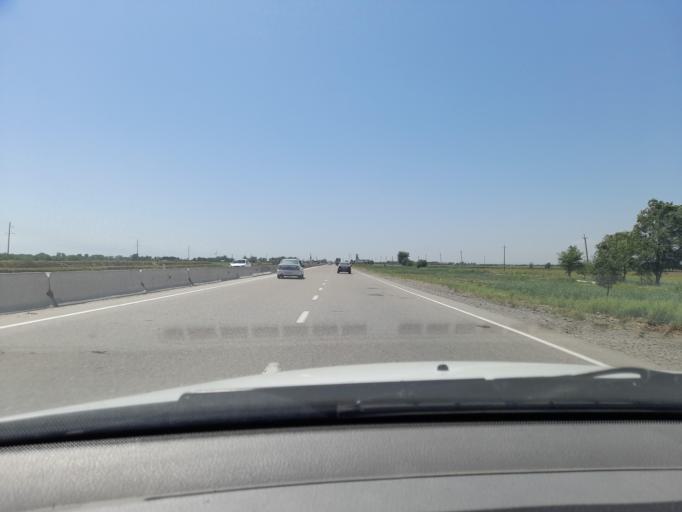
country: UZ
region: Jizzax
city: Dustlik
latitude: 40.3765
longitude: 68.1610
